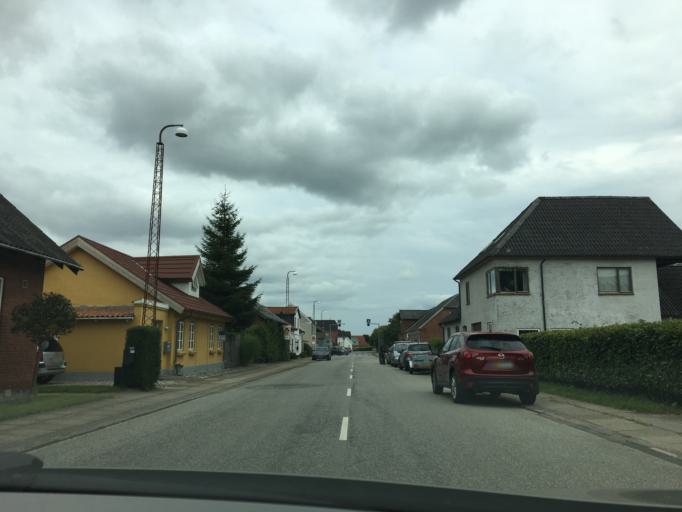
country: DK
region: South Denmark
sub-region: Vejle Kommune
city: Jelling
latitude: 55.7024
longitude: 9.3777
